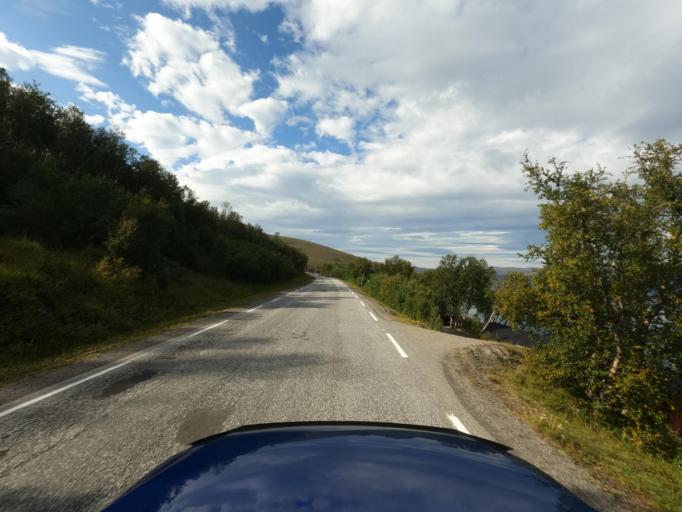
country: NO
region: Finnmark Fylke
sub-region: Kvalsund
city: Kvalsund
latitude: 70.4907
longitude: 24.1249
